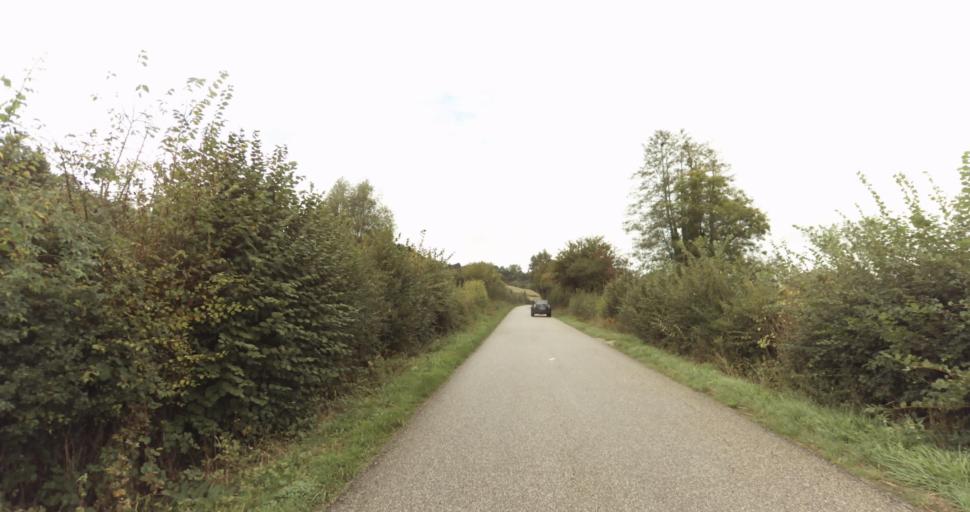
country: FR
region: Lower Normandy
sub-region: Departement de l'Orne
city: Vimoutiers
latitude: 48.8723
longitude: 0.2227
